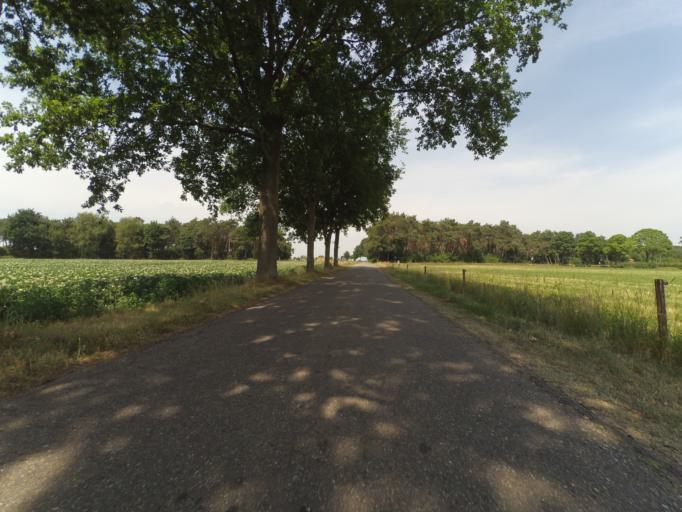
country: BE
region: Flanders
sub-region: Provincie Antwerpen
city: Wuustwezel
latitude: 51.4160
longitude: 4.5911
